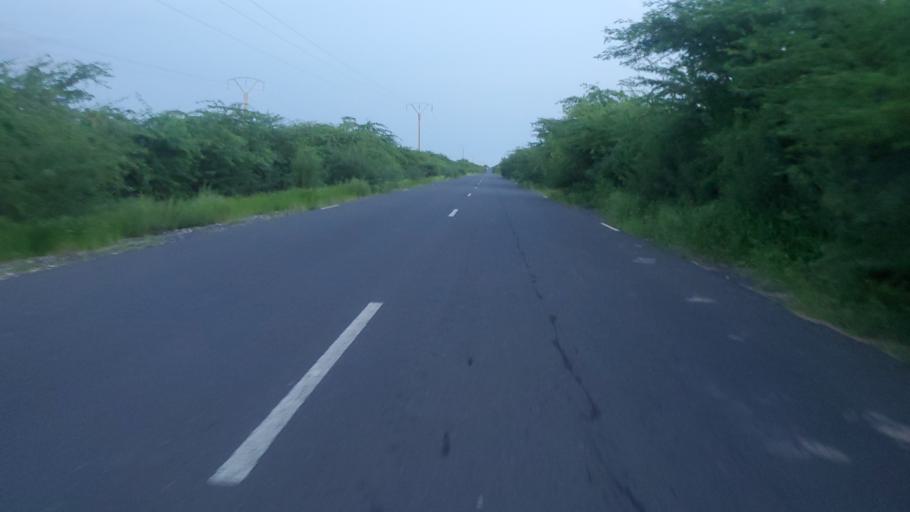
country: SN
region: Saint-Louis
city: Saint-Louis
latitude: 16.0858
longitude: -16.3942
